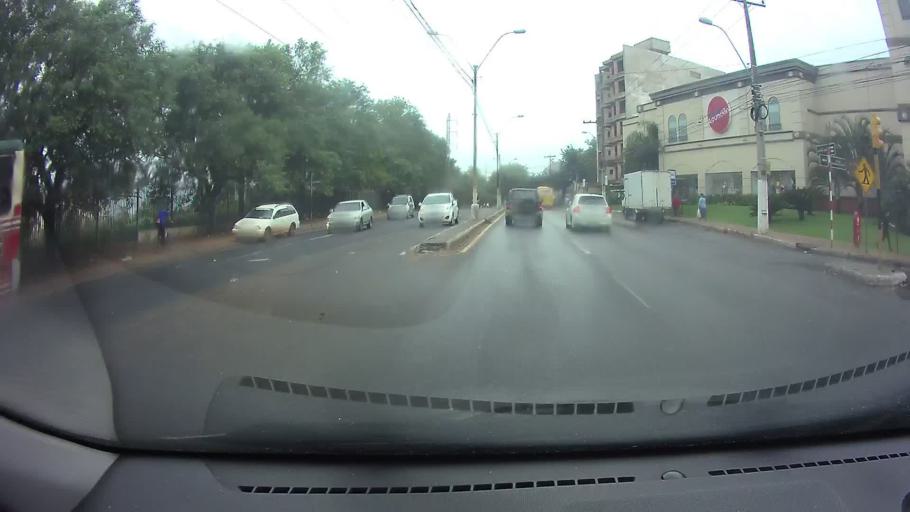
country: PY
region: Central
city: Fernando de la Mora
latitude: -25.3243
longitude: -57.5209
